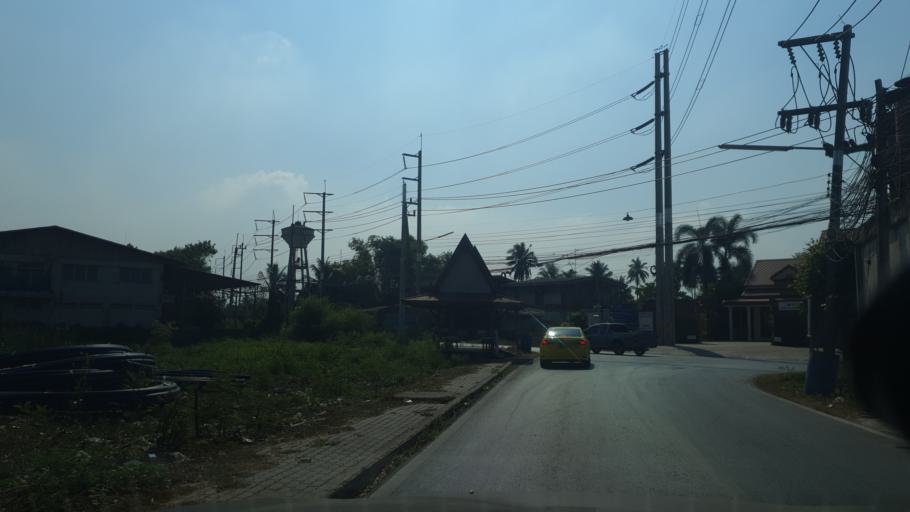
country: TH
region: Nakhon Pathom
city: Salaya
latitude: 13.7798
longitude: 100.2700
